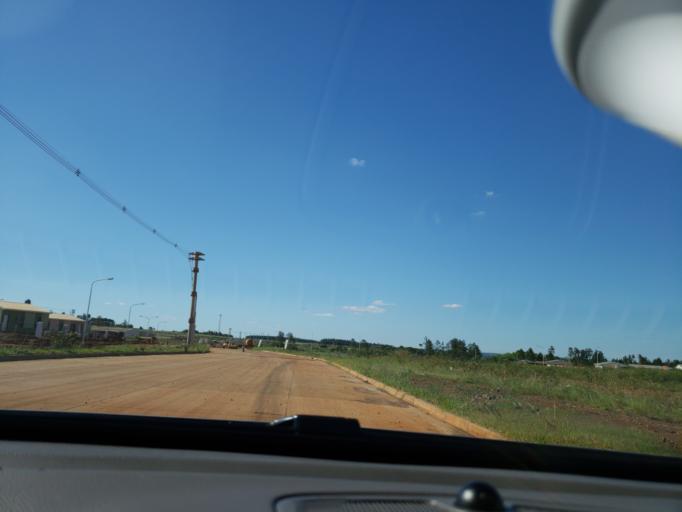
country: AR
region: Misiones
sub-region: Departamento de Capital
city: Posadas
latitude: -27.4004
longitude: -55.9891
